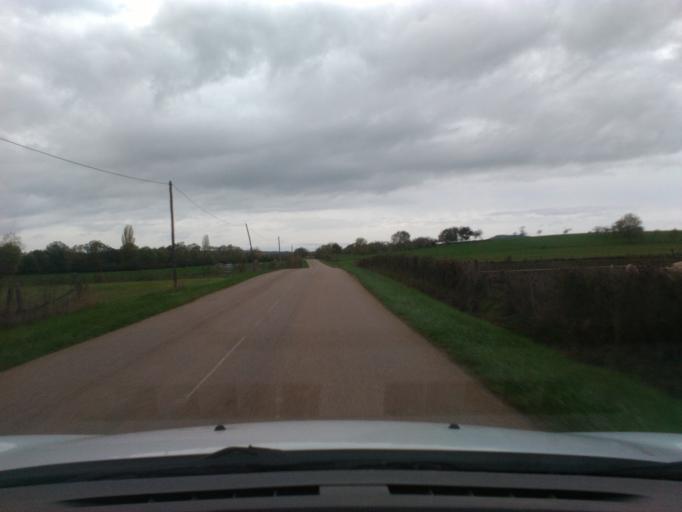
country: FR
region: Lorraine
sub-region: Departement des Vosges
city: Mirecourt
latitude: 48.3492
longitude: 6.0949
